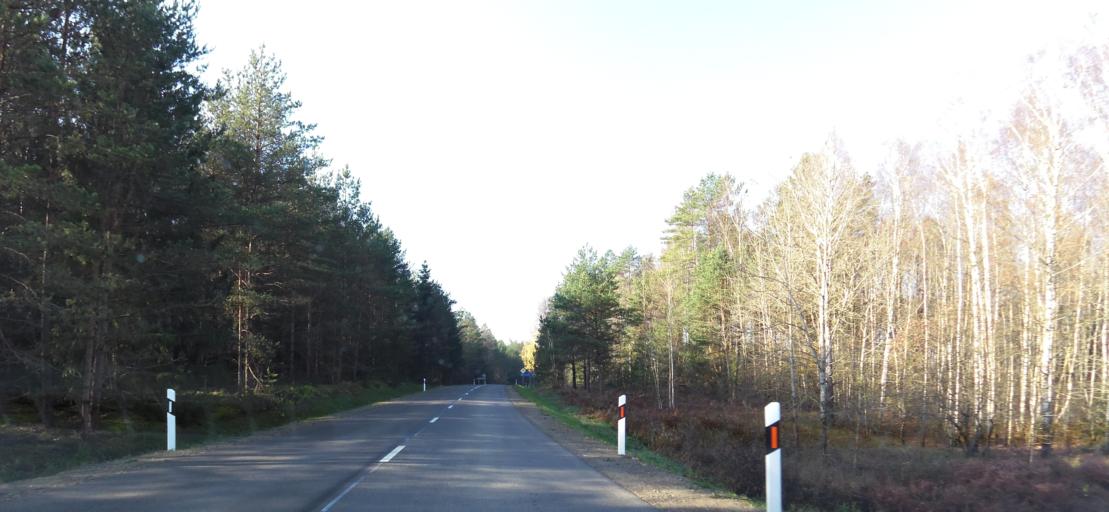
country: LT
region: Vilnius County
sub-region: Trakai
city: Rudiskes
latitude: 54.5086
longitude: 24.8727
